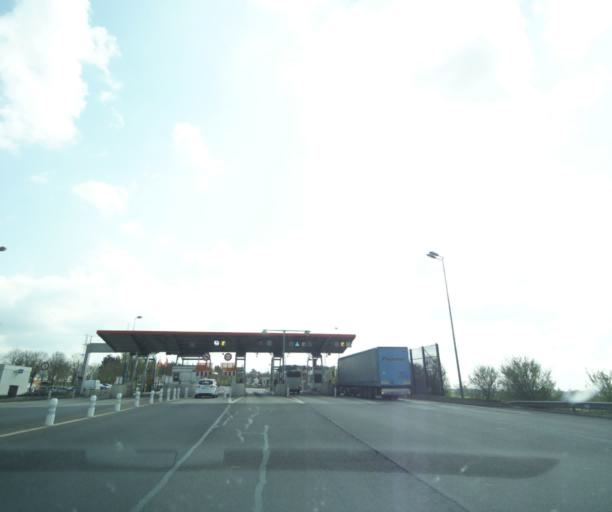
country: FR
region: Auvergne
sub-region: Departement de l'Allier
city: Montmarault
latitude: 46.3281
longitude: 2.9664
